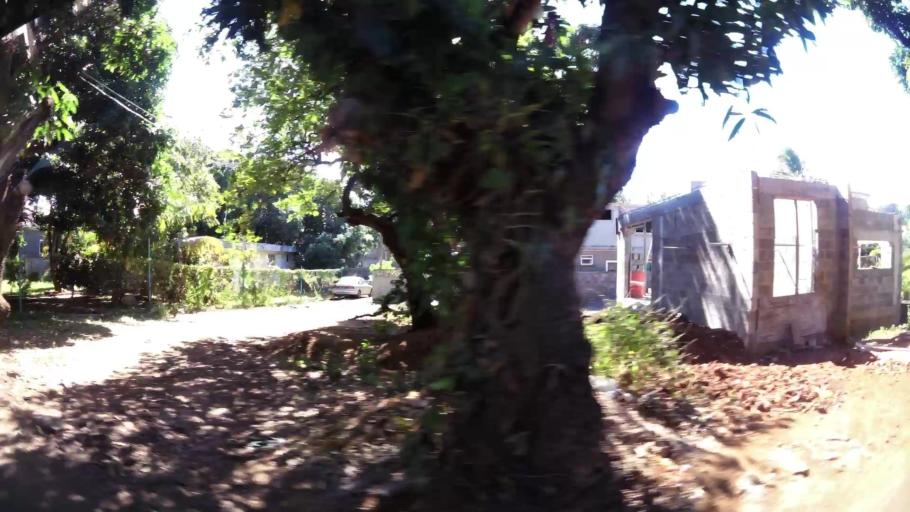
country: MU
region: Black River
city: Cascavelle
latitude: -20.2639
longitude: 57.4158
